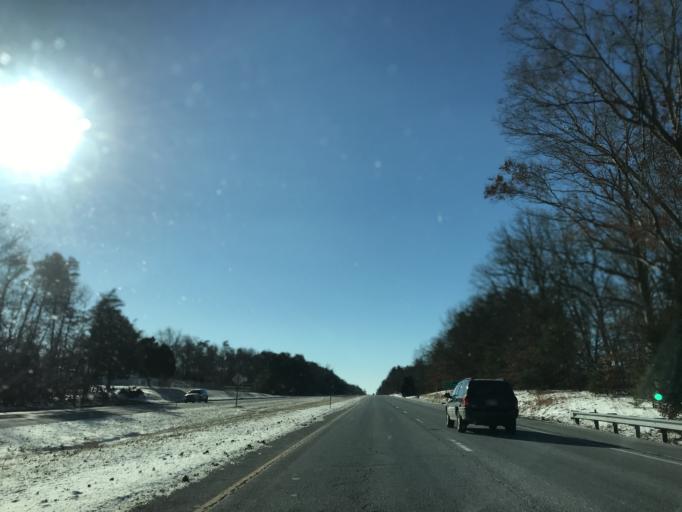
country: US
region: Maryland
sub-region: Charles County
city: La Plata
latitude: 38.4868
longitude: -76.9880
